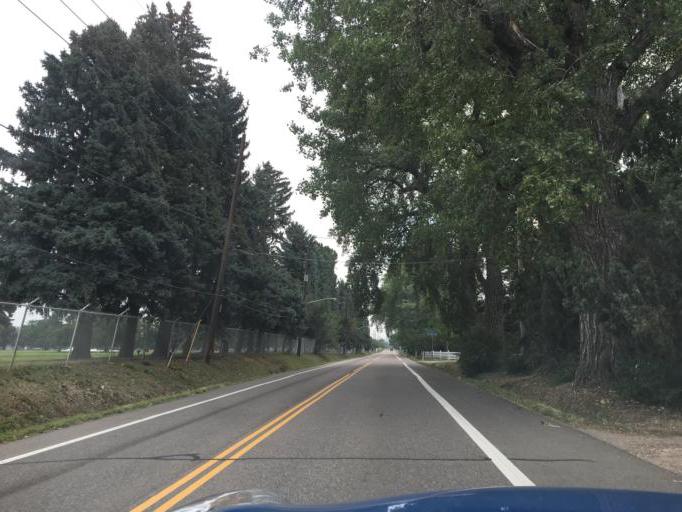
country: US
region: Colorado
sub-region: Jefferson County
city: Wheat Ridge
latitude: 39.7548
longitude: -105.0937
